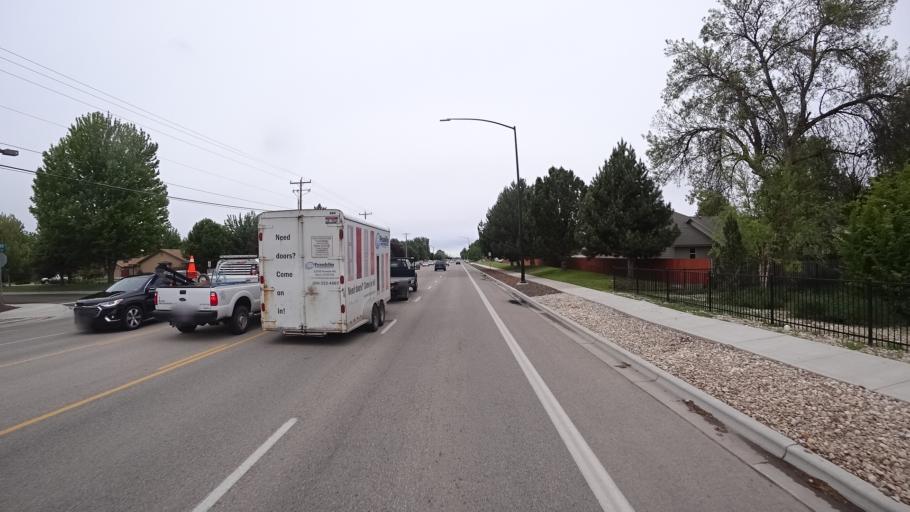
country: US
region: Idaho
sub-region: Ada County
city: Meridian
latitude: 43.6338
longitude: -116.3771
